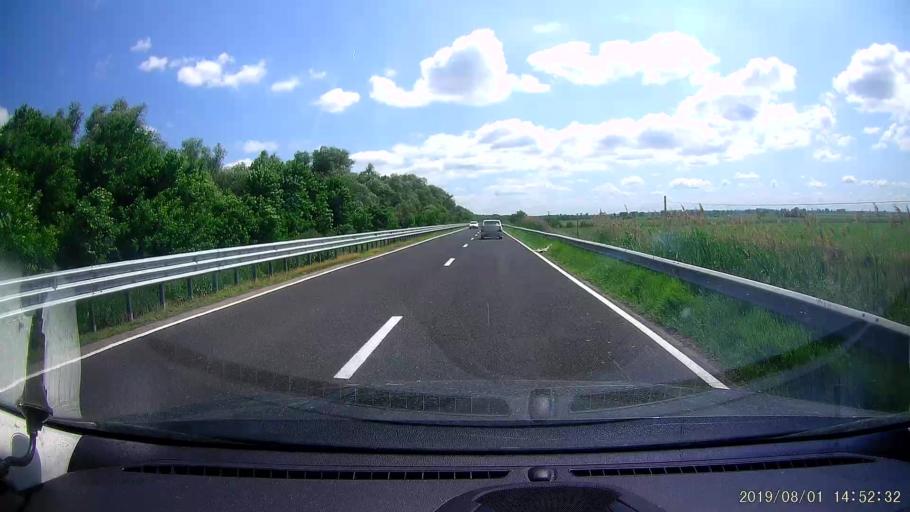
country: RO
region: Braila
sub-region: Comuna Vadeni
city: Vadeni
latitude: 45.3531
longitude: 28.0105
